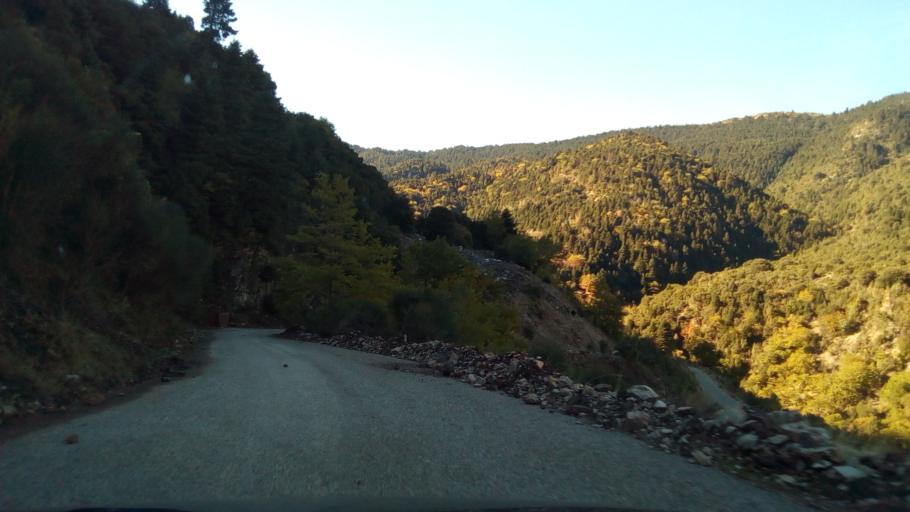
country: GR
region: West Greece
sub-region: Nomos Aitolias kai Akarnanias
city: Nafpaktos
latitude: 38.5506
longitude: 21.8525
